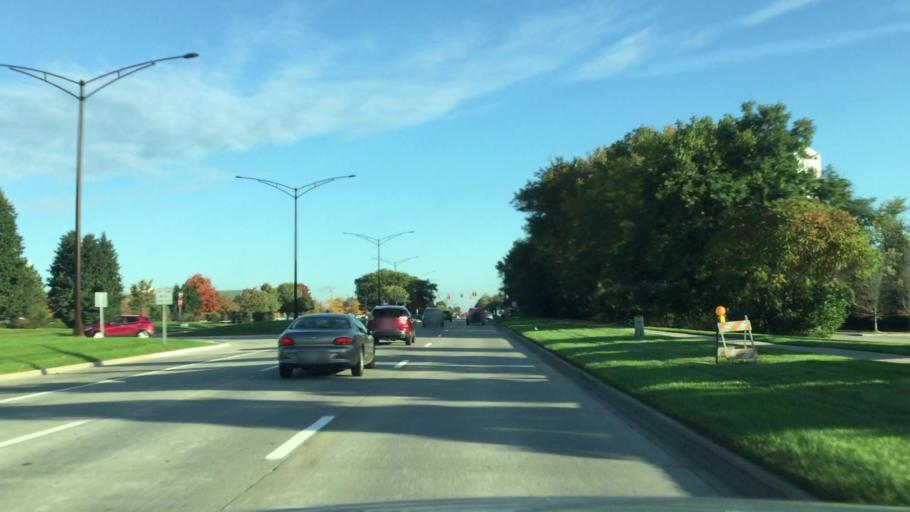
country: US
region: Michigan
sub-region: Oakland County
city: Troy
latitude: 42.5938
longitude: -83.1686
